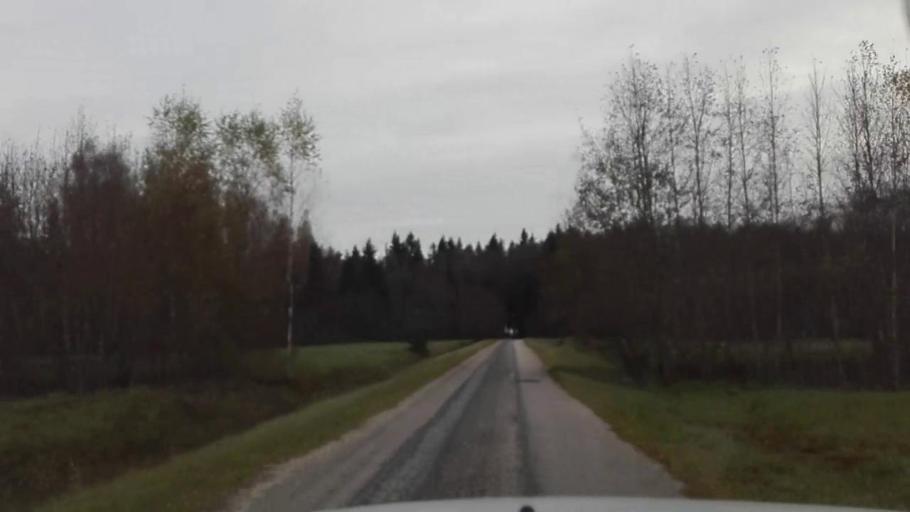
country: EE
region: Jogevamaa
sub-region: Poltsamaa linn
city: Poltsamaa
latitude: 58.4090
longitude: 26.0099
